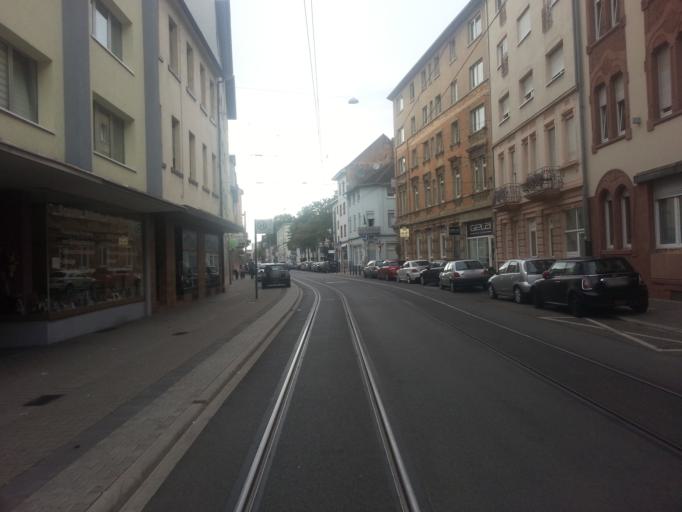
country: DE
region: Baden-Wuerttemberg
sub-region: Karlsruhe Region
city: Mannheim
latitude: 49.4755
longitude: 8.4810
